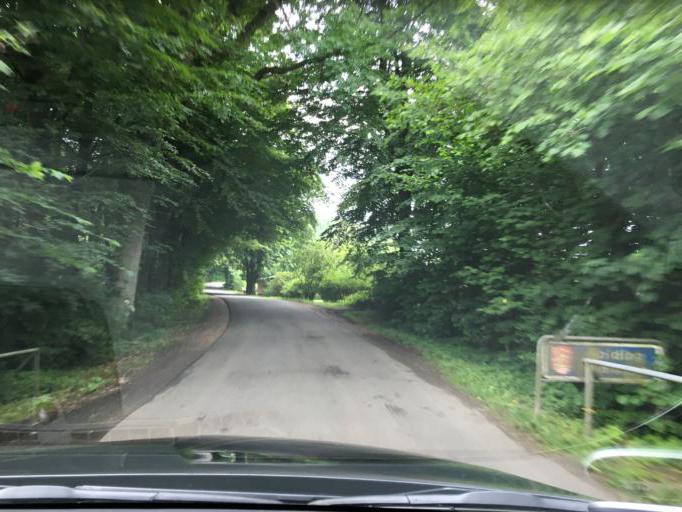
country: DK
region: South Denmark
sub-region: Vejle Kommune
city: Vejle
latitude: 55.6173
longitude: 9.5148
